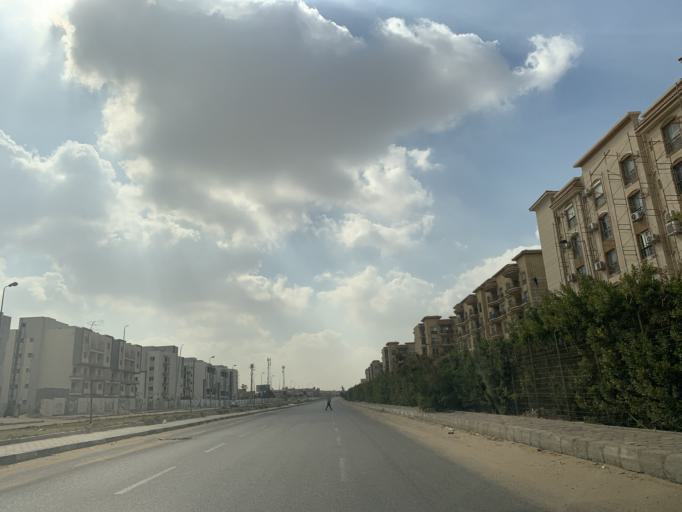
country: EG
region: Muhafazat al Qalyubiyah
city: Al Khankah
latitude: 30.0664
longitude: 31.5195
